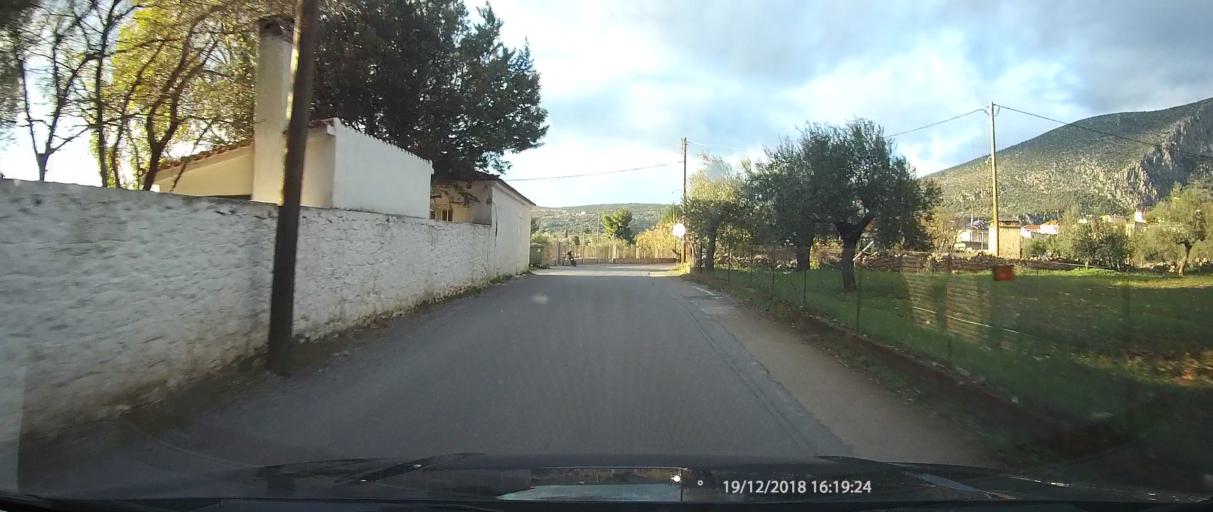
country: GR
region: Peloponnese
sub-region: Nomos Lakonias
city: Kato Glikovrisi
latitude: 36.9318
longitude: 22.8222
